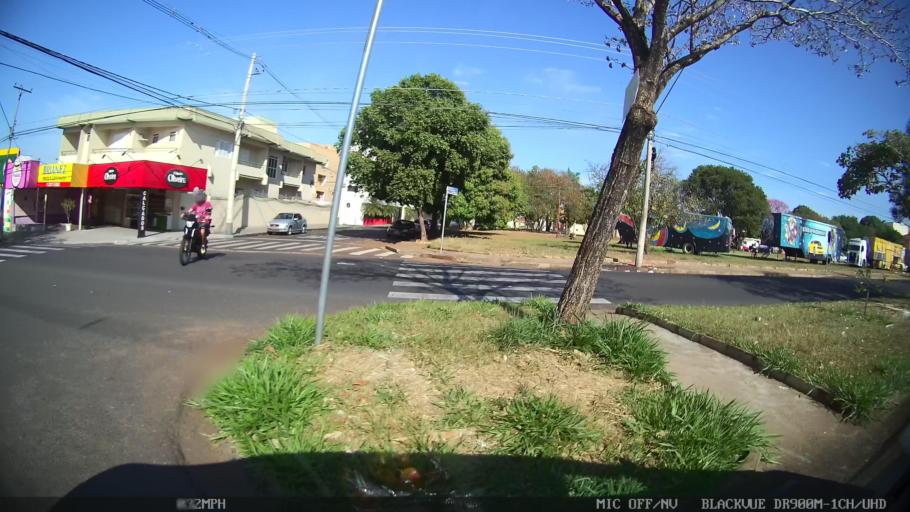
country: BR
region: Sao Paulo
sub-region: Sao Jose Do Rio Preto
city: Sao Jose do Rio Preto
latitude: -20.7992
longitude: -49.4101
